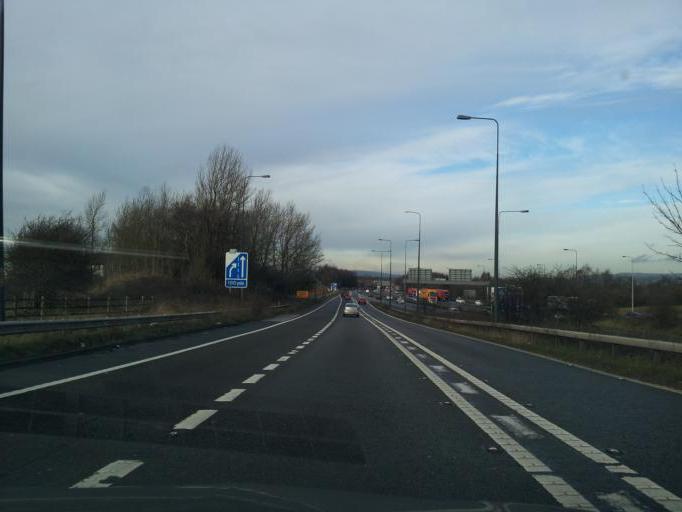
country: GB
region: England
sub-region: Borough of Bury
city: Prestwich
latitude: 53.5511
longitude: -2.2626
